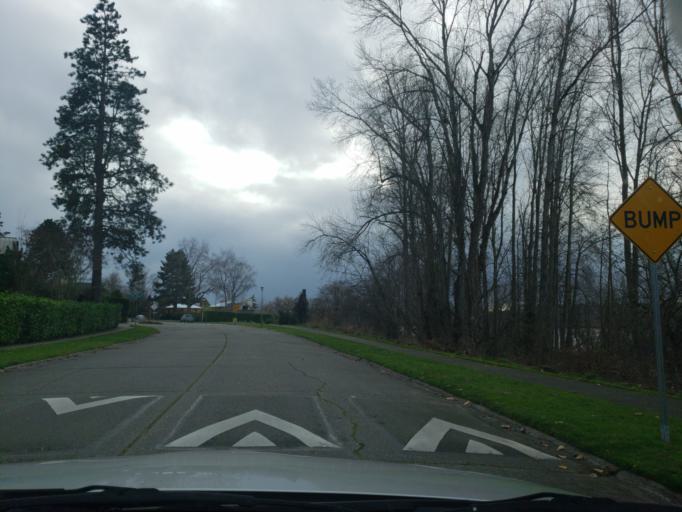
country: US
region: Washington
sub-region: King County
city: Seattle
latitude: 47.6575
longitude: -122.2868
